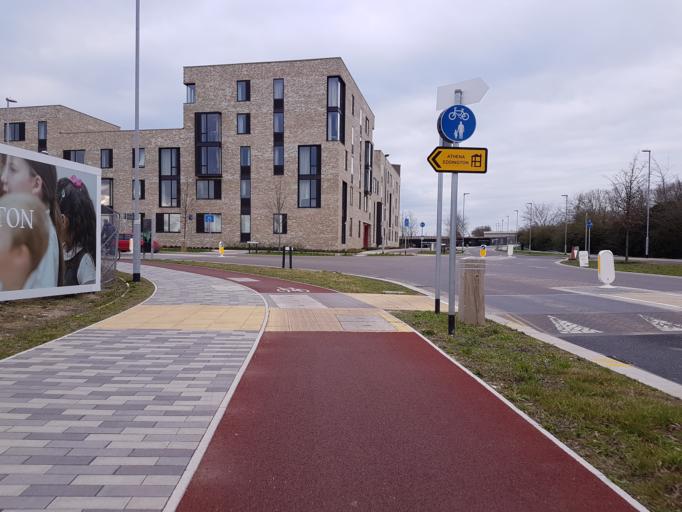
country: GB
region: England
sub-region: Cambridgeshire
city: Girton
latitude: 52.2160
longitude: 0.0872
